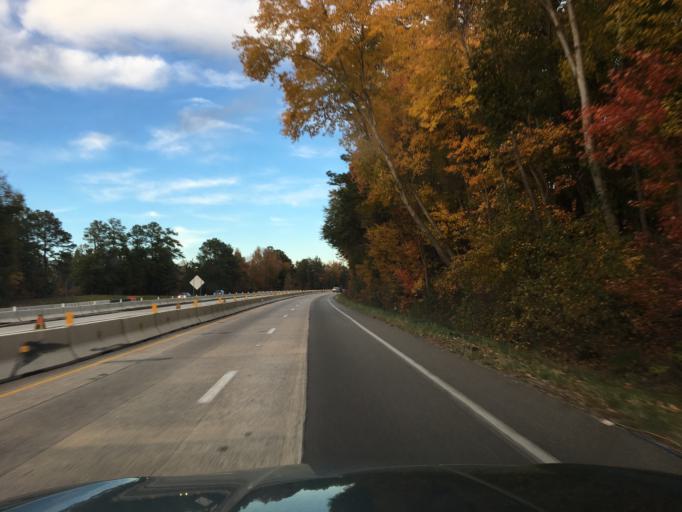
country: US
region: South Carolina
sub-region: Lexington County
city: Oak Grove
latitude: 33.9993
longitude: -81.1737
